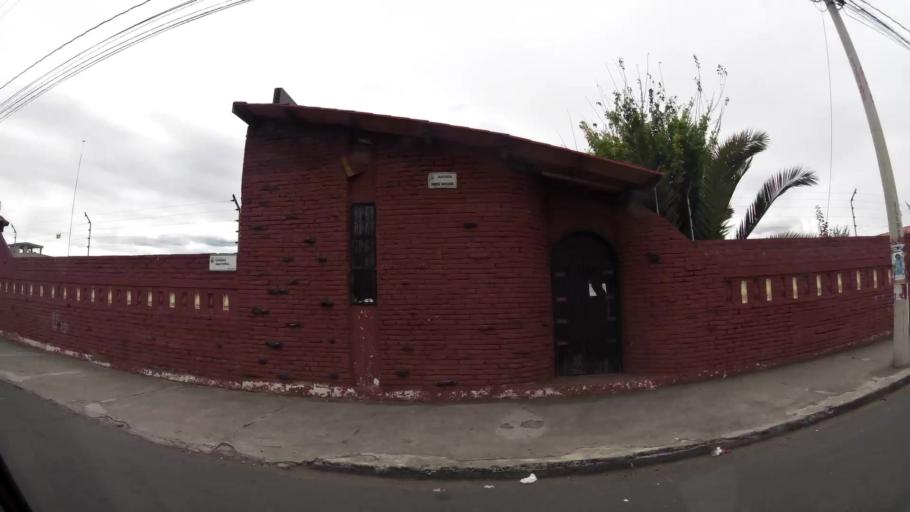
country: EC
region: Cotopaxi
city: Latacunga
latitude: -0.9422
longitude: -78.6118
